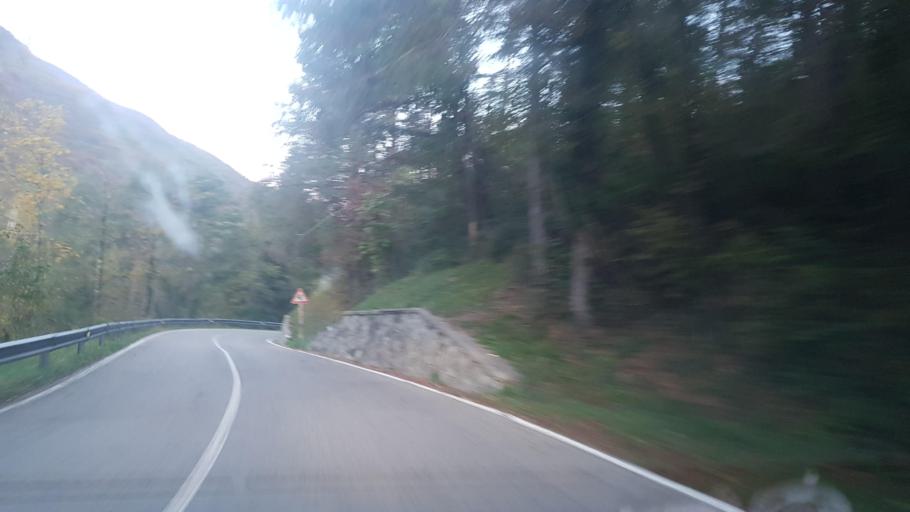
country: IT
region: Friuli Venezia Giulia
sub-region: Provincia di Udine
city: Chiaulis
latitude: 46.3837
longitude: 12.9669
